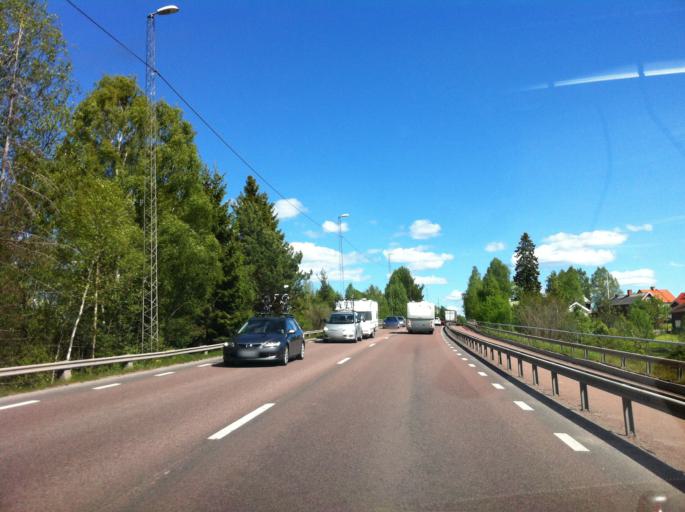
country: SE
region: Dalarna
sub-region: Mora Kommun
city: Mora
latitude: 61.0097
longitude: 14.5752
